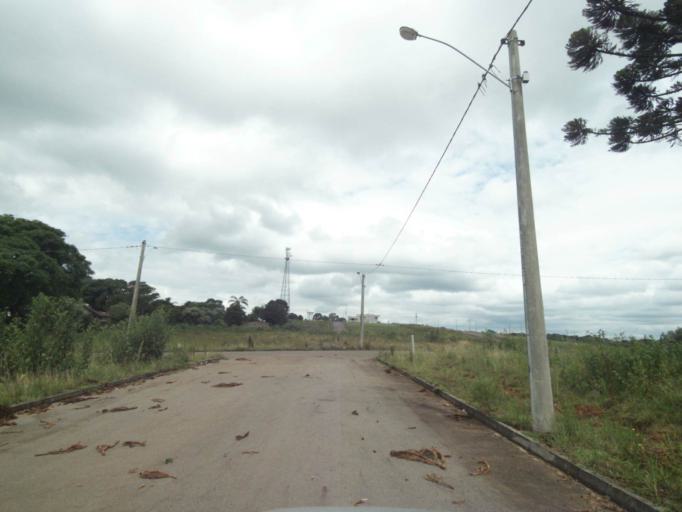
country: BR
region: Rio Grande do Sul
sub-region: Lagoa Vermelha
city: Lagoa Vermelha
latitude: -28.2178
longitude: -51.5185
